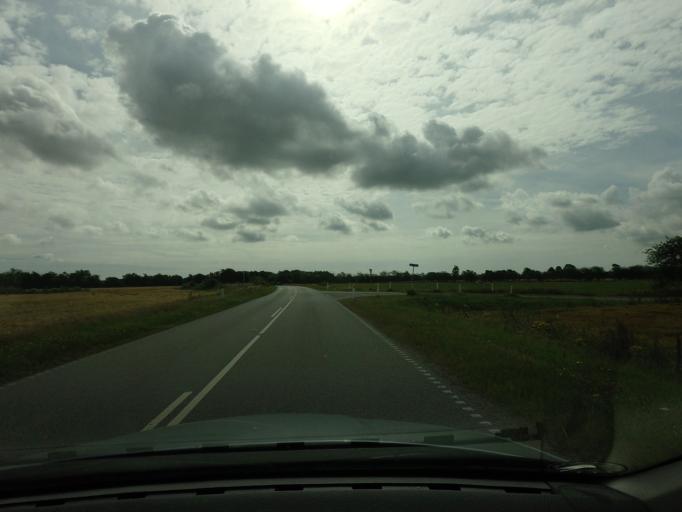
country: DK
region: North Denmark
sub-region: Bronderslev Kommune
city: Dronninglund
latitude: 57.2818
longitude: 10.3401
